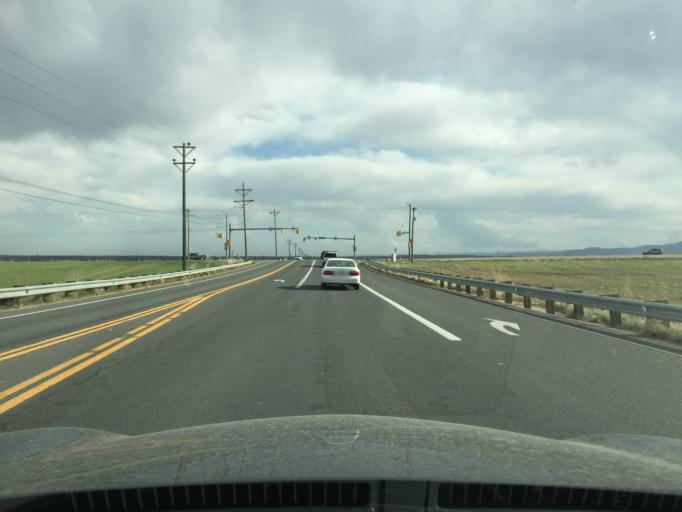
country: US
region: Colorado
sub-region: Boulder County
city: Niwot
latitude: 40.0887
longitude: -105.1315
